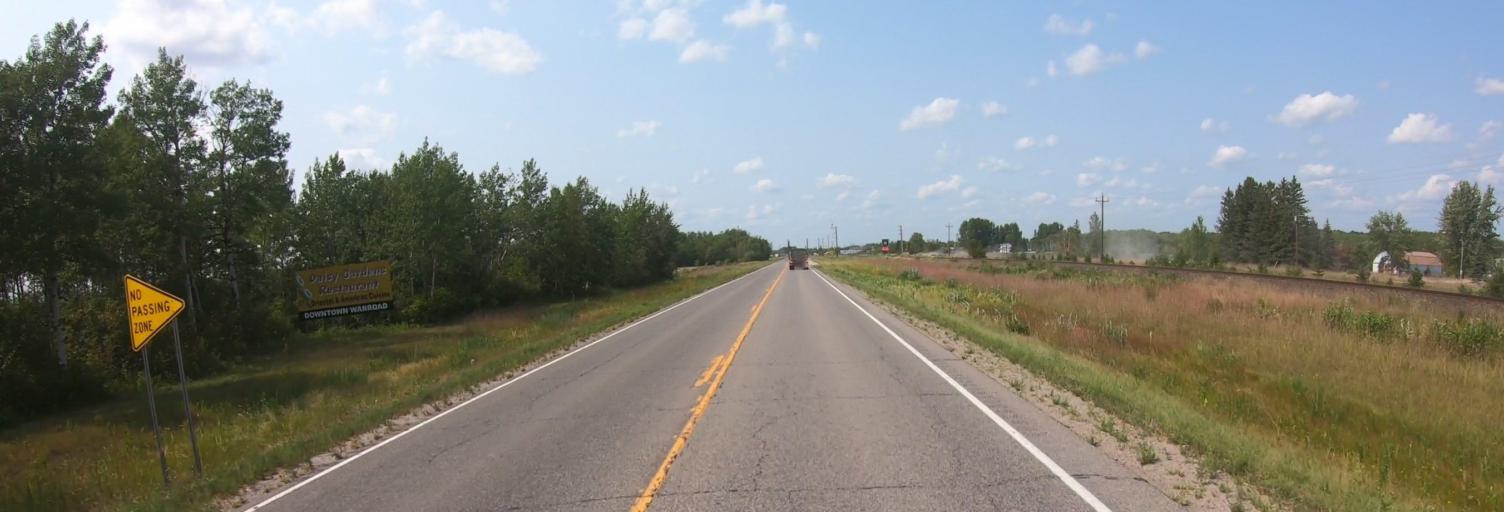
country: US
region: Minnesota
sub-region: Roseau County
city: Warroad
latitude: 48.8900
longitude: -95.3045
